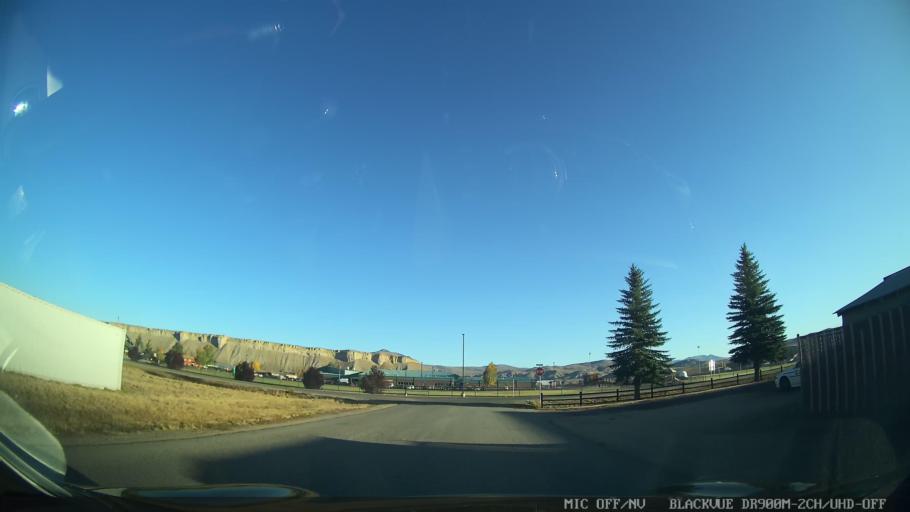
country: US
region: Colorado
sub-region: Grand County
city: Kremmling
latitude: 40.0580
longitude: -106.3794
